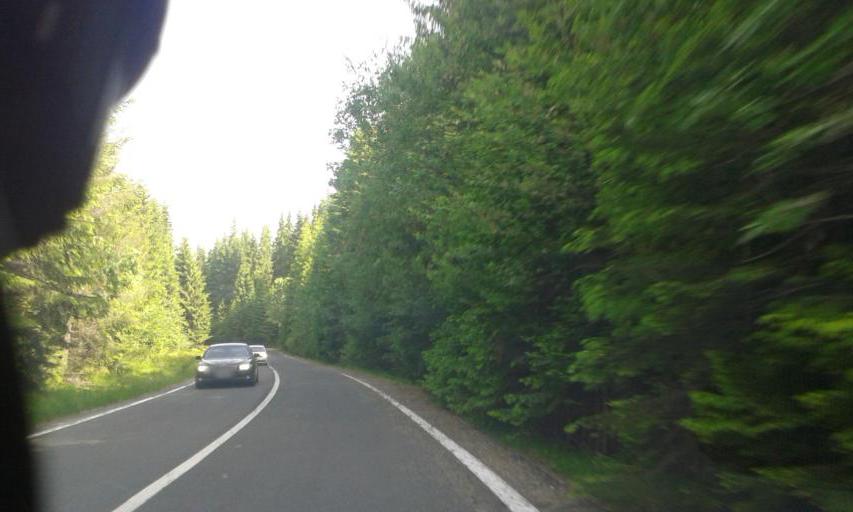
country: RO
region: Alba
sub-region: Comuna Sugag
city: Sugag
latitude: 45.5660
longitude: 23.6180
